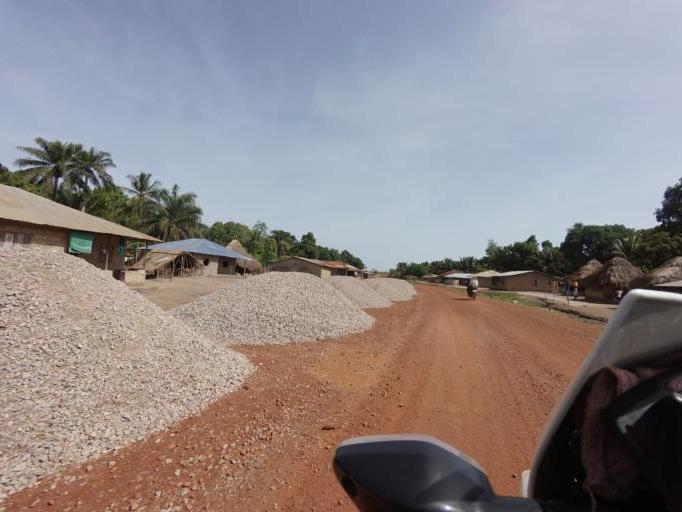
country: SL
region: Northern Province
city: Makeni
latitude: 9.0685
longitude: -12.1768
